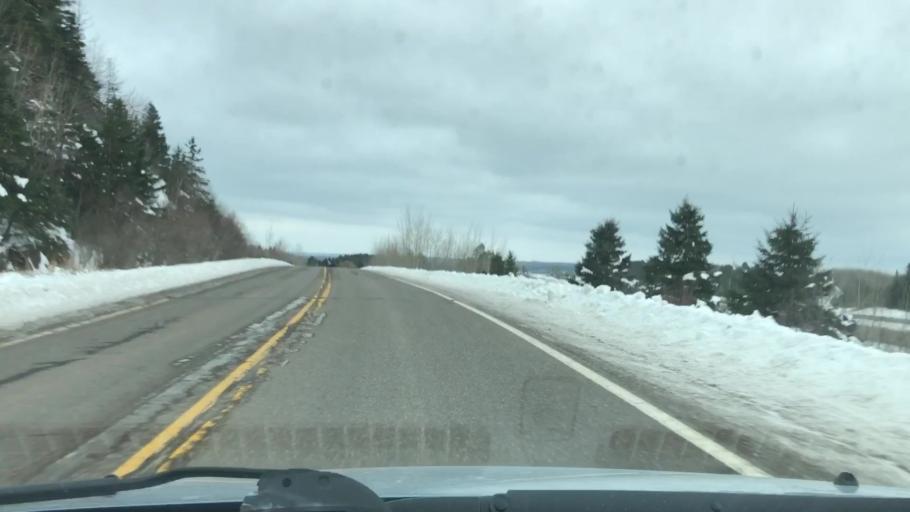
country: US
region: Minnesota
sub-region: Saint Louis County
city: Proctor
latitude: 46.7098
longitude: -92.2739
